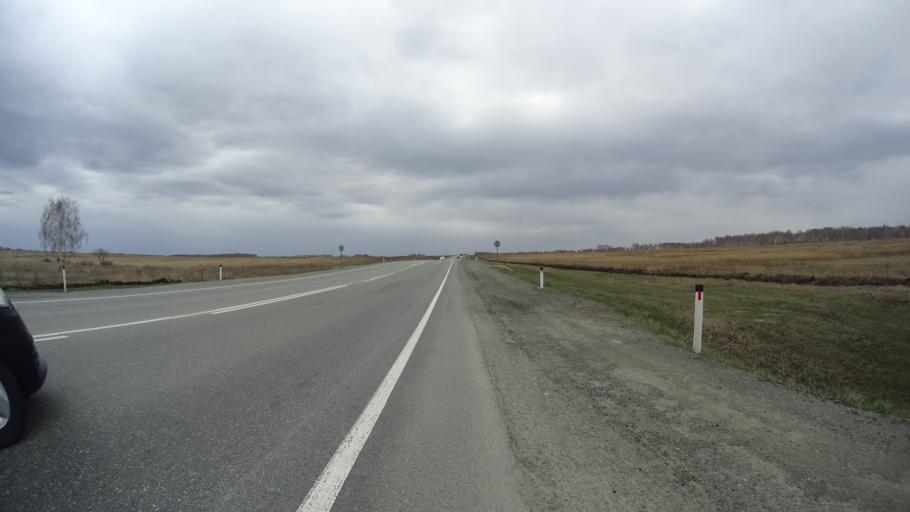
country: RU
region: Chelyabinsk
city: Yemanzhelinsk
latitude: 54.7109
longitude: 61.2600
